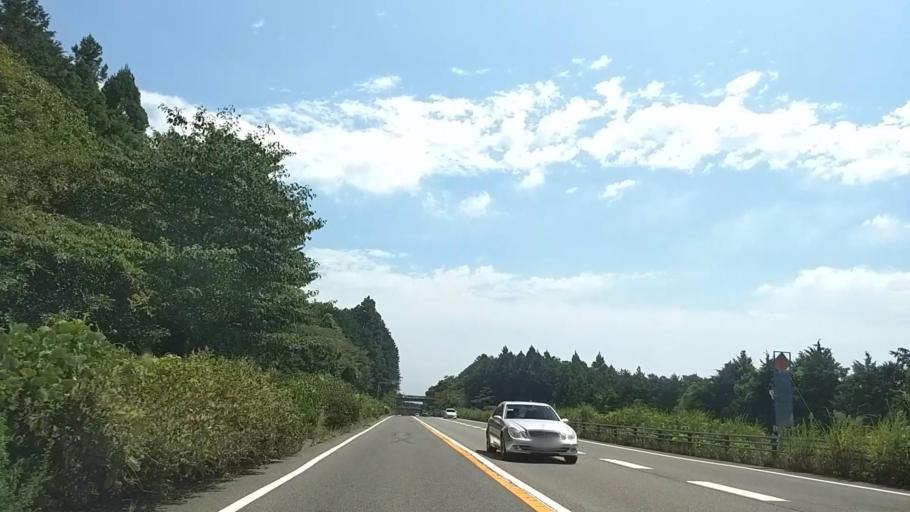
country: JP
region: Shizuoka
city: Fujinomiya
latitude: 35.2935
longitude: 138.6067
